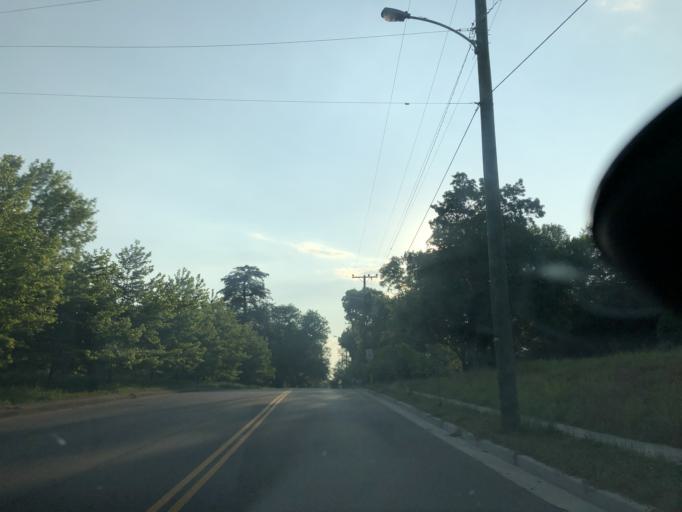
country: US
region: Tennessee
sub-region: Davidson County
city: Oak Hill
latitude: 36.1172
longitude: -86.7920
